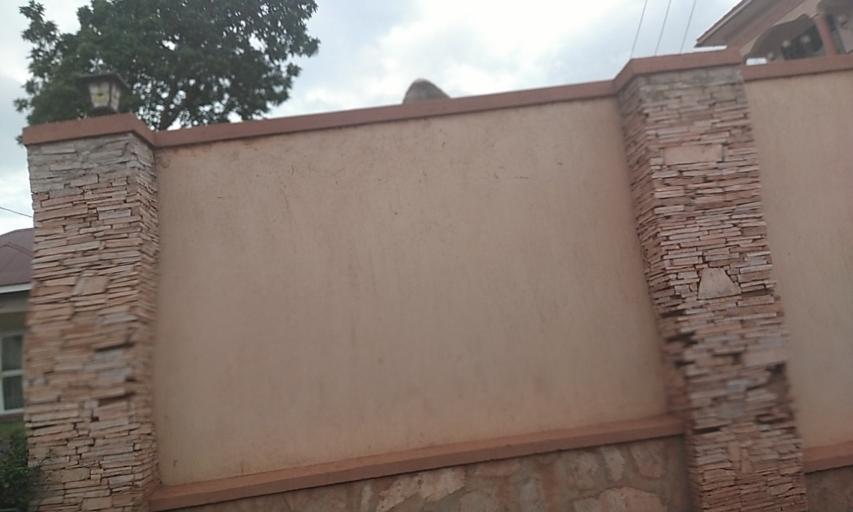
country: UG
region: Central Region
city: Kampala Central Division
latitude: 0.3524
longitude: 32.6057
